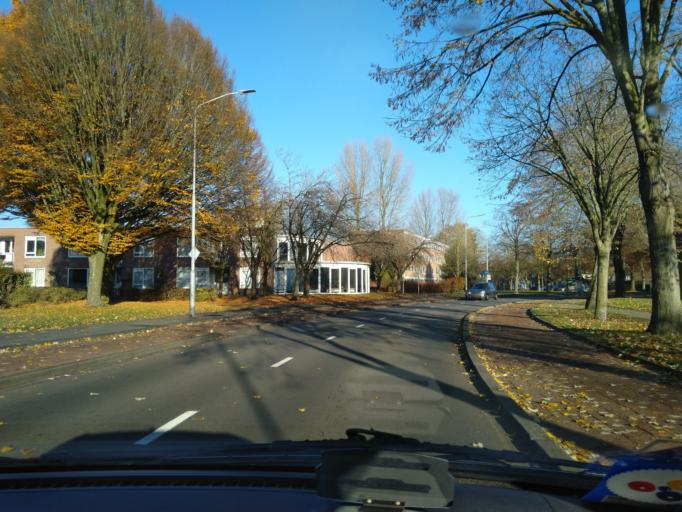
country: NL
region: Drenthe
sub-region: Gemeente Assen
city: Assen
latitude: 53.0037
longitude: 6.5484
